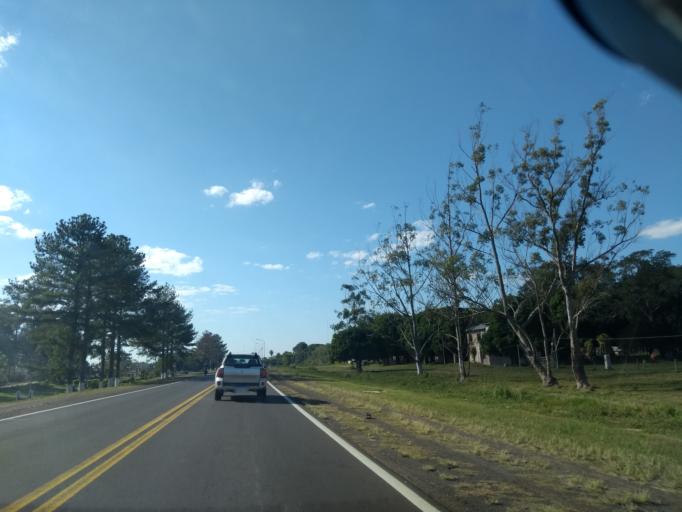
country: AR
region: Corrientes
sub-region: Departamento de Itati
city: Itati
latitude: -27.3660
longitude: -58.3033
